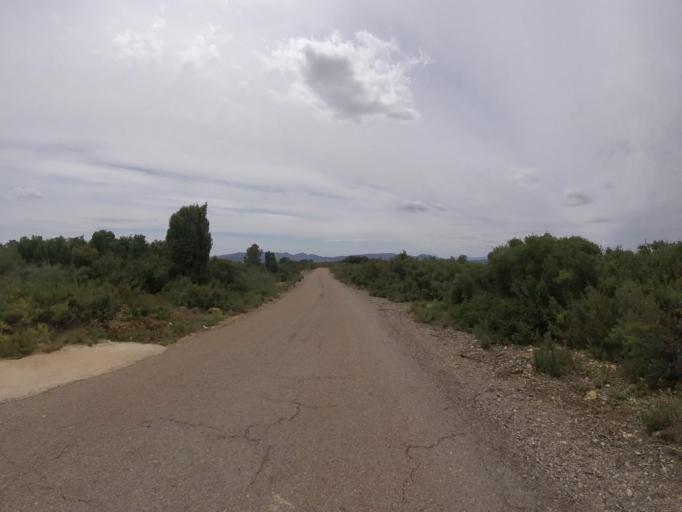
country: ES
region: Valencia
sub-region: Provincia de Castello
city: Sierra-Engarceran
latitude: 40.2416
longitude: -0.0264
